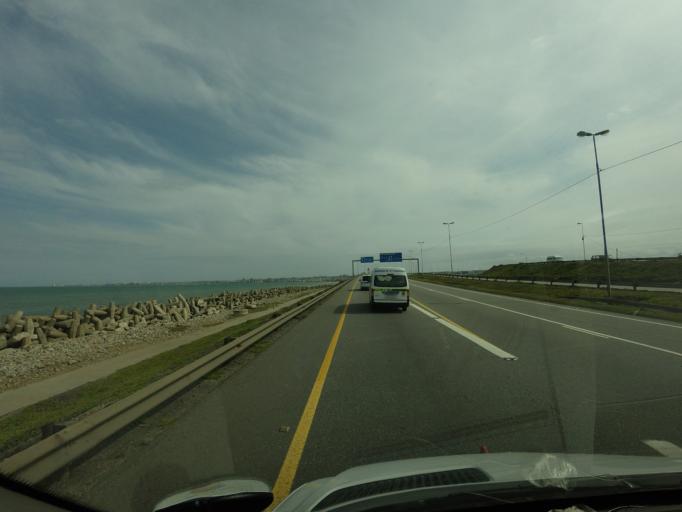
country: ZA
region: Eastern Cape
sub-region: Nelson Mandela Bay Metropolitan Municipality
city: Port Elizabeth
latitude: -33.9114
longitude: 25.6161
